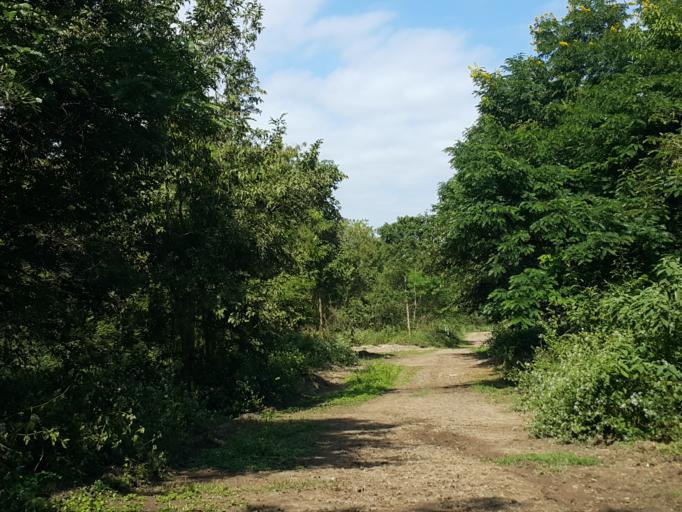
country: TH
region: Lampang
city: Mae Mo
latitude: 18.3382
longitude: 99.7687
